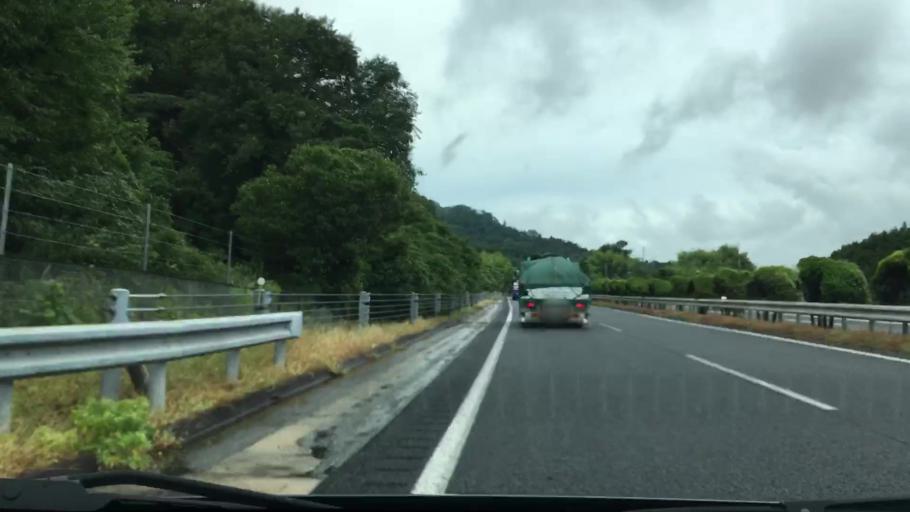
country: JP
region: Hyogo
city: Himeji
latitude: 34.9557
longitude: 134.7188
